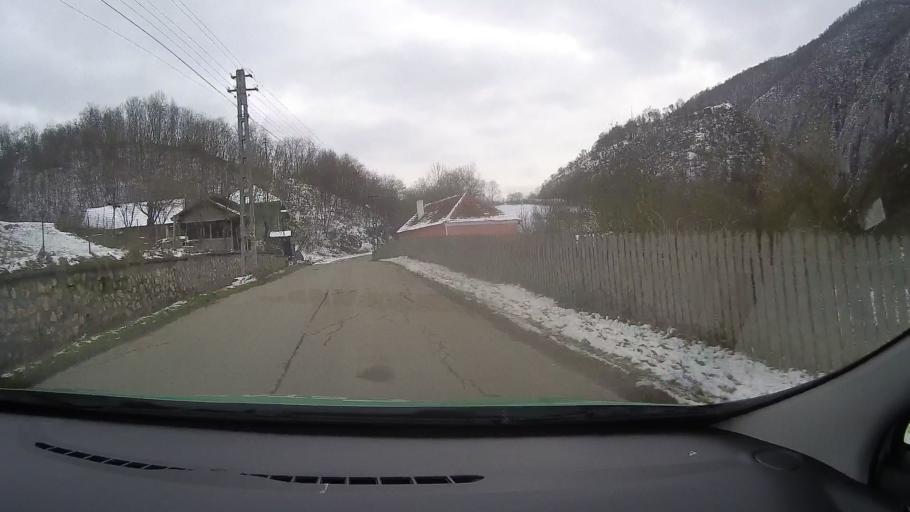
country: RO
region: Hunedoara
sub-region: Comuna Balsa
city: Balsa
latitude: 46.0198
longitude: 23.1457
